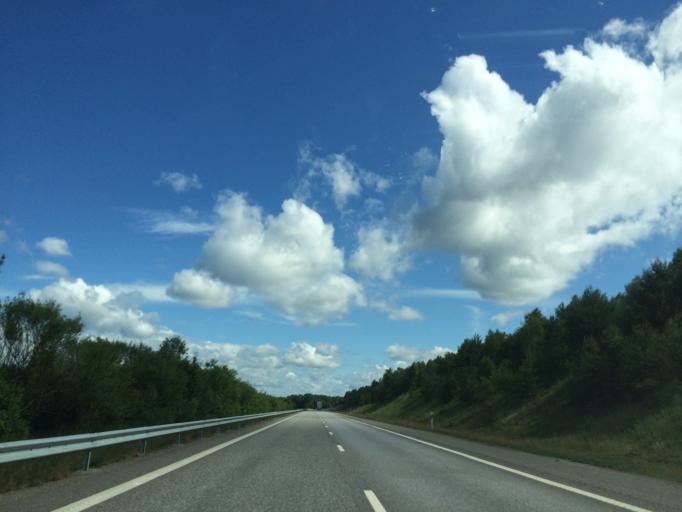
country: SE
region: Kronoberg
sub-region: Markaryds Kommun
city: Stromsnasbruk
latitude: 56.6329
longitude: 13.7931
